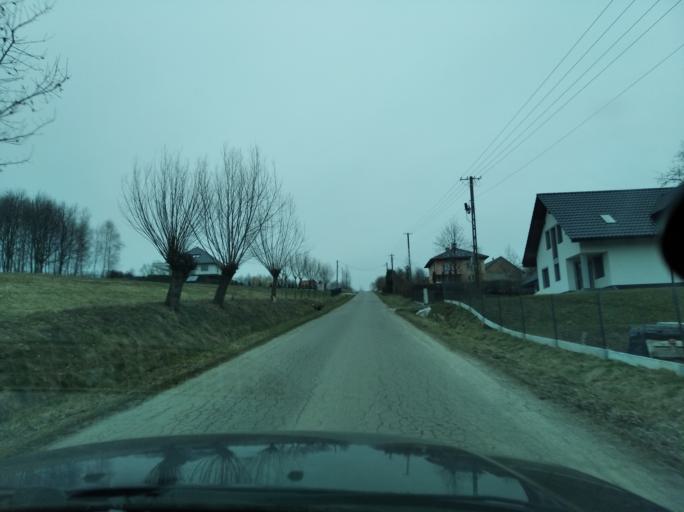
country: PL
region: Subcarpathian Voivodeship
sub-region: Powiat rzeszowski
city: Chmielnik
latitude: 49.9784
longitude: 22.1460
